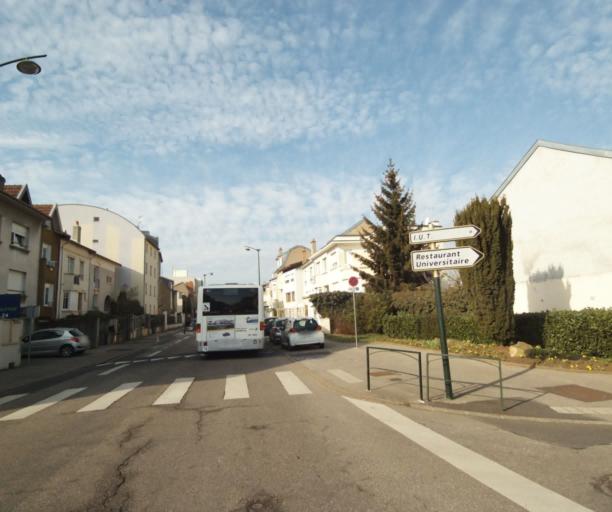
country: FR
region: Lorraine
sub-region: Departement de Meurthe-et-Moselle
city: Laxou
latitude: 48.6815
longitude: 6.1612
